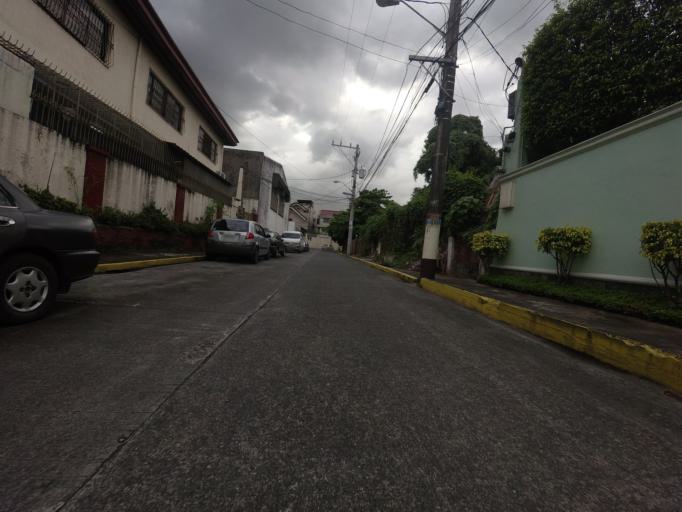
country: PH
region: Metro Manila
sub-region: Mandaluyong
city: Mandaluyong City
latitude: 14.5918
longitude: 121.0425
